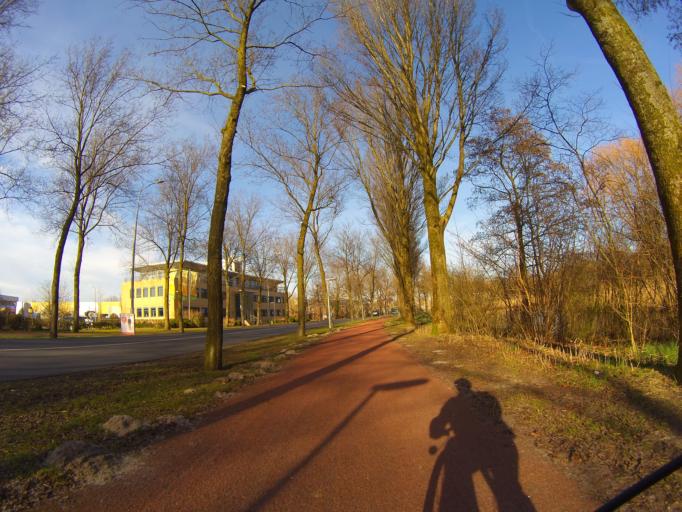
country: NL
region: North Holland
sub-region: Gemeente Huizen
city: Huizen
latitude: 52.3062
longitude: 5.2485
